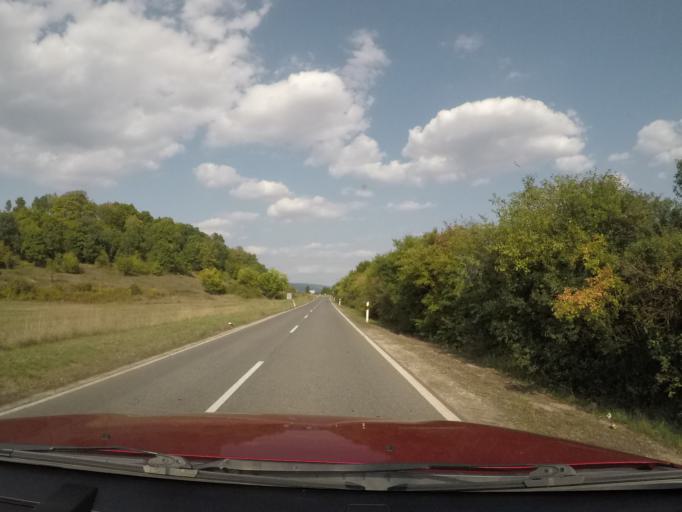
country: HU
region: Borsod-Abauj-Zemplen
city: Szendro
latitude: 48.5261
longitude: 20.7265
